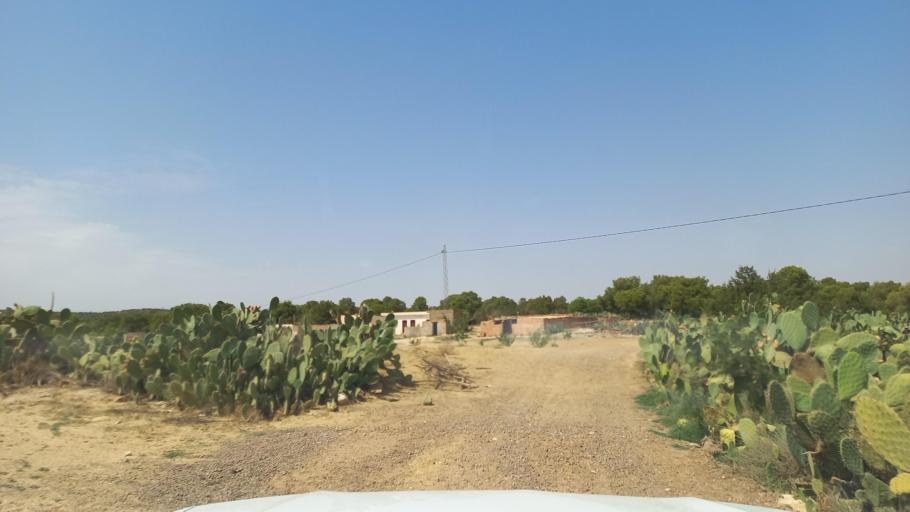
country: TN
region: Al Qasrayn
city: Sbiba
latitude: 35.3899
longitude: 8.9459
